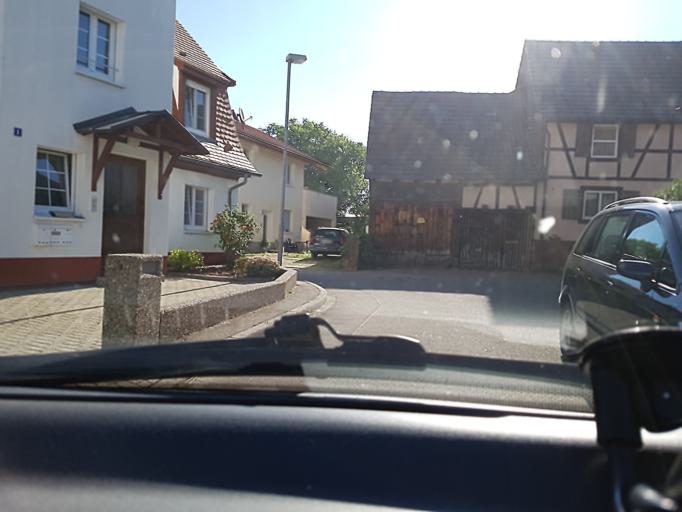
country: DE
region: Baden-Wuerttemberg
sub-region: Freiburg Region
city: Willstatt
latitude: 48.5695
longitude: 7.8682
